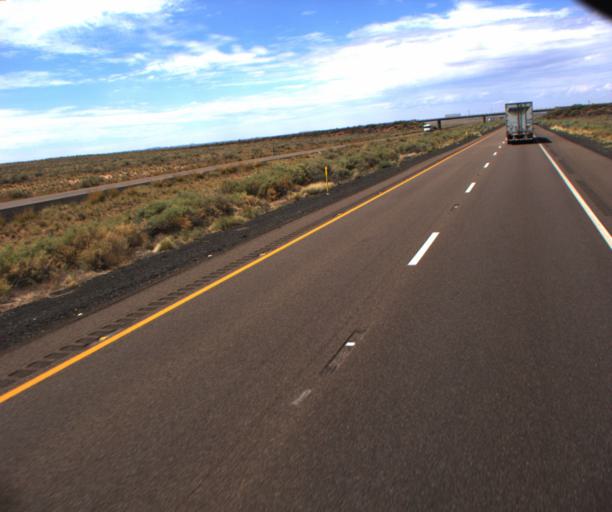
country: US
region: Arizona
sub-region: Navajo County
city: Holbrook
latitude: 35.0499
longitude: -109.8000
